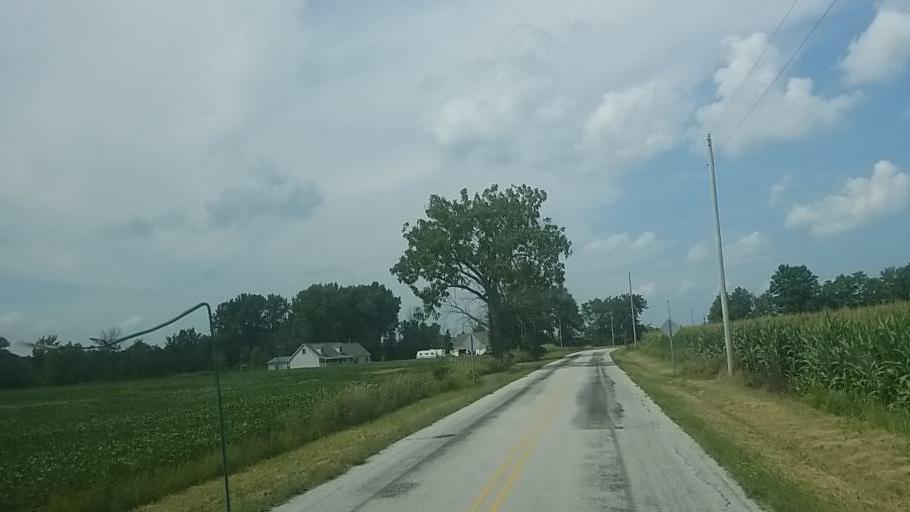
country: US
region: Ohio
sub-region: Hardin County
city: Kenton
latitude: 40.7471
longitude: -83.6022
